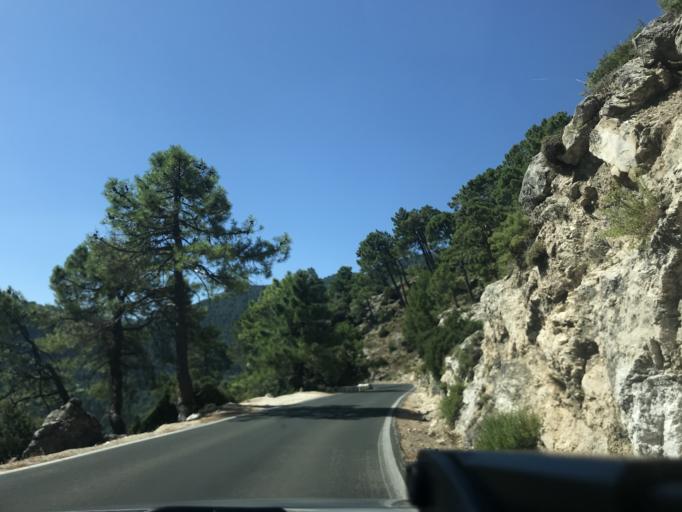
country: ES
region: Andalusia
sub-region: Provincia de Jaen
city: La Iruela
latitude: 37.9290
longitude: -2.9490
